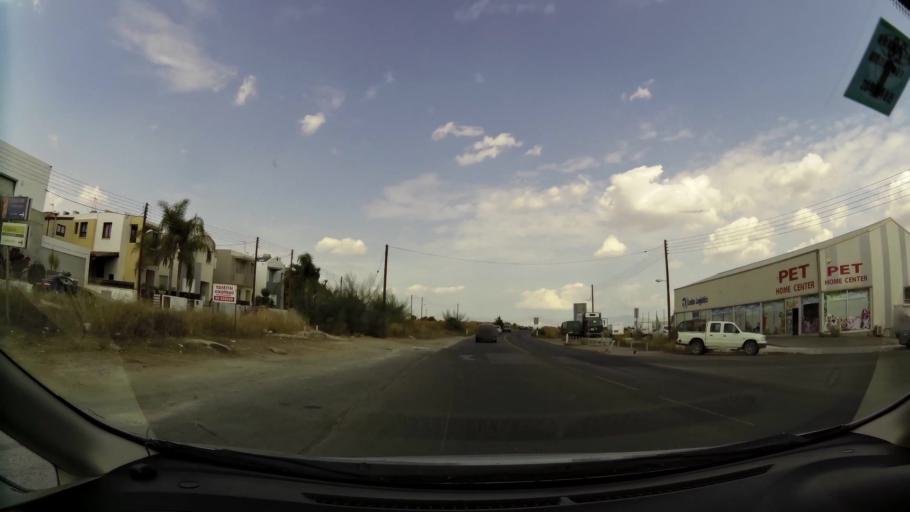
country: CY
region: Lefkosia
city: Tseri
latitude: 35.0983
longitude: 33.3270
